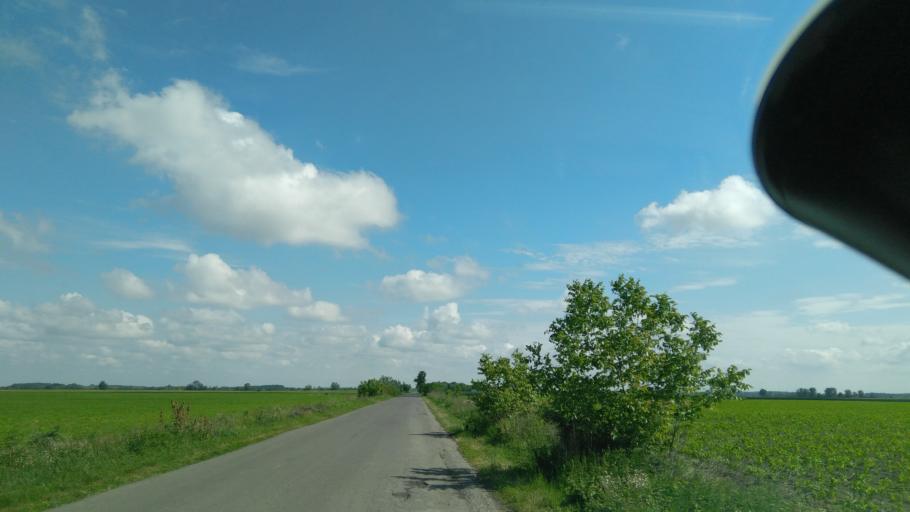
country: HU
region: Bekes
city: Bekes
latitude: 46.8010
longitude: 21.1427
